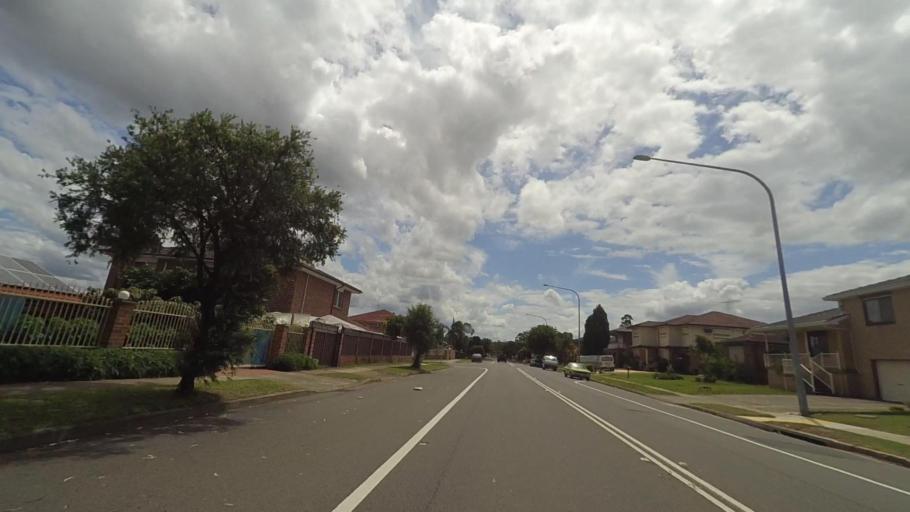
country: AU
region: New South Wales
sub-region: Fairfield
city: Fairfield Heights
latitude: -33.8678
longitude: 150.9164
